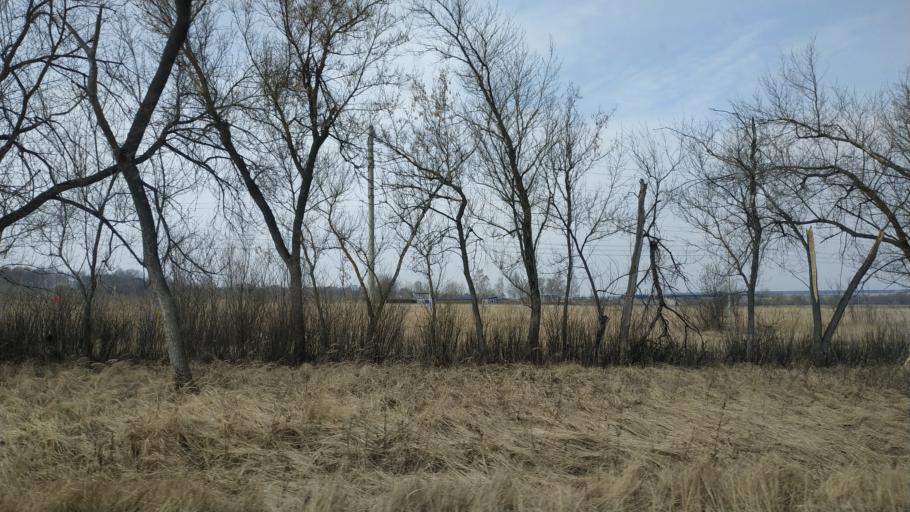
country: RU
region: Moskovskaya
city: Bronnitsy
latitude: 55.3936
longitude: 38.3537
